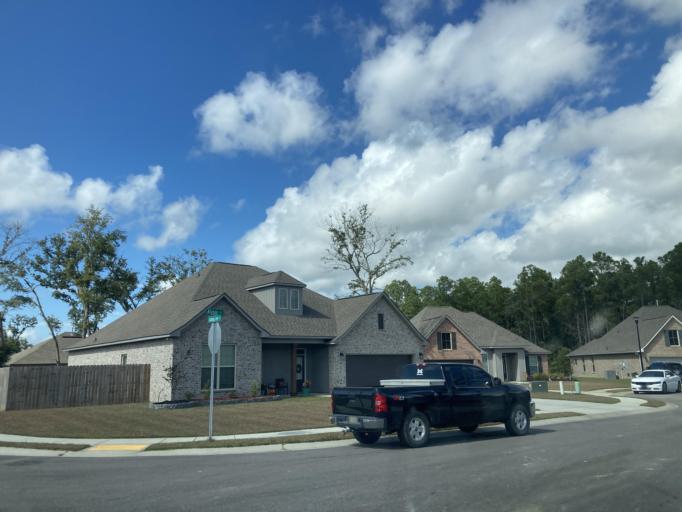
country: US
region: Mississippi
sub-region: Jackson County
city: Gulf Hills
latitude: 30.4524
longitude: -88.8265
